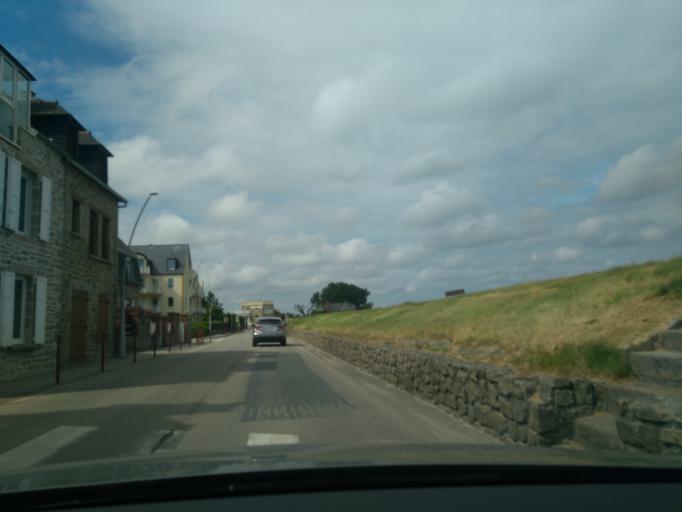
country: FR
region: Lower Normandy
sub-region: Departement de la Manche
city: Saint-Vaast-la-Hougue
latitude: 49.5913
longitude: -1.2667
